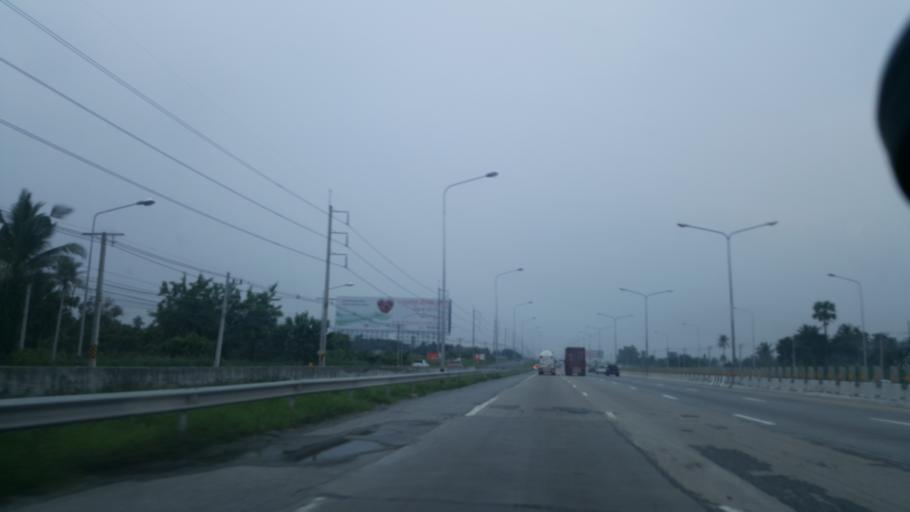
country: TH
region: Chon Buri
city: Si Racha
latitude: 13.2067
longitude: 101.0041
